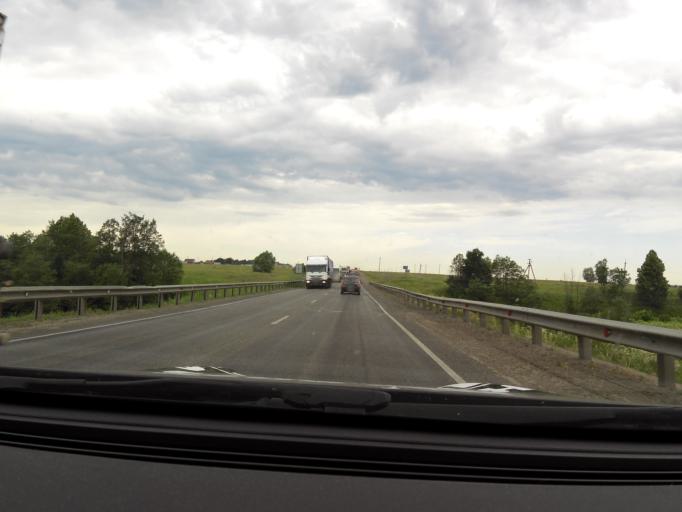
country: RU
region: Bashkortostan
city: Kudeyevskiy
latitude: 54.8170
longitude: 56.7715
